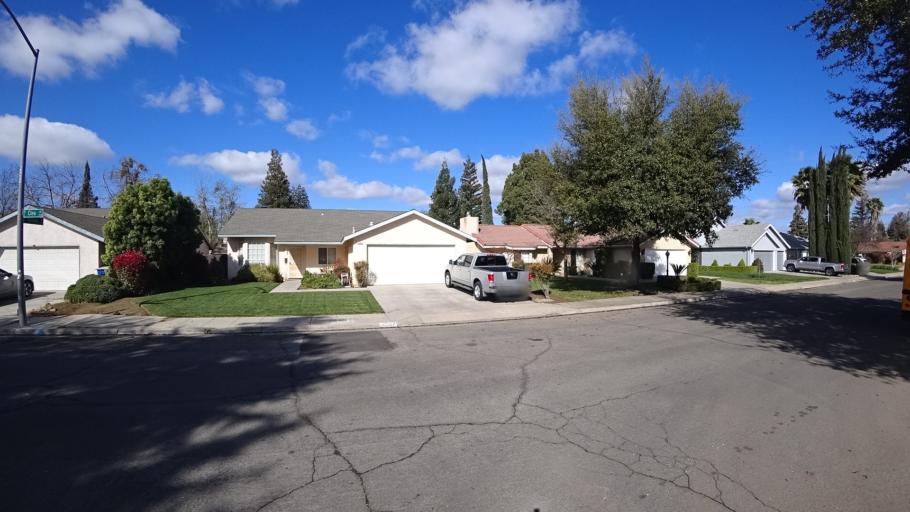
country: US
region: California
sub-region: Fresno County
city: West Park
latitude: 36.8292
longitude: -119.8824
